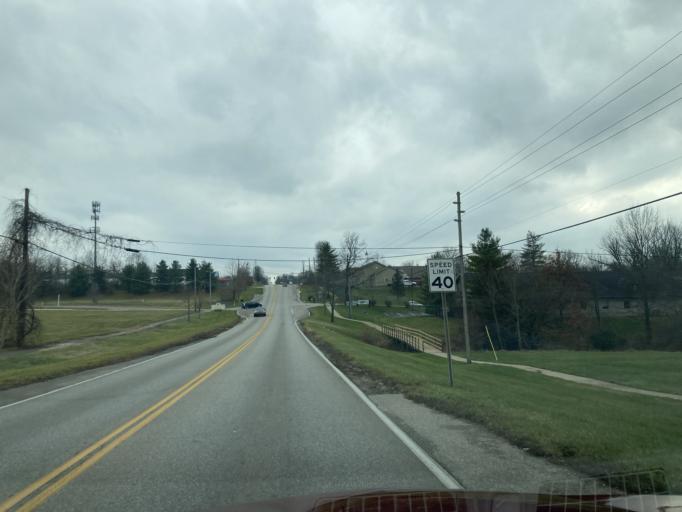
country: US
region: Indiana
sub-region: Monroe County
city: Bloomington
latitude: 39.1251
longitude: -86.5314
